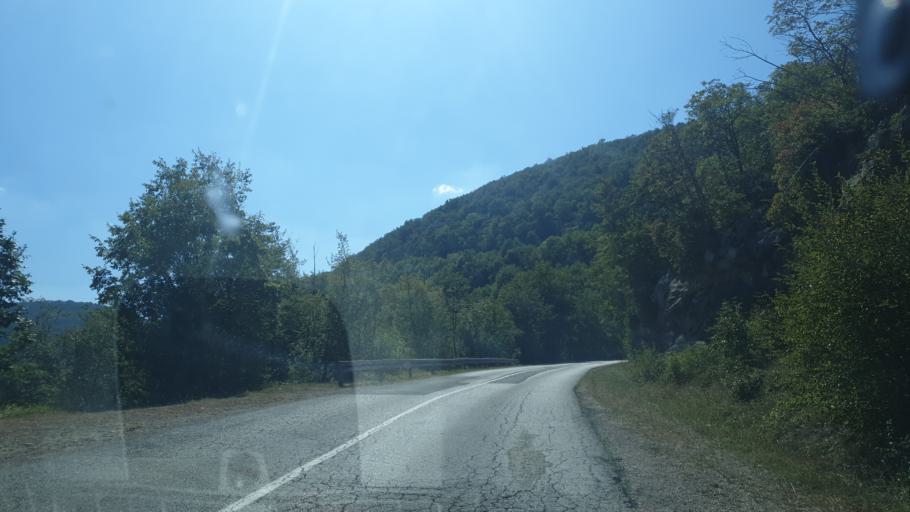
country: RS
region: Central Serbia
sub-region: Kolubarski Okrug
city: Mionica
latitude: 44.1522
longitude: 20.0227
